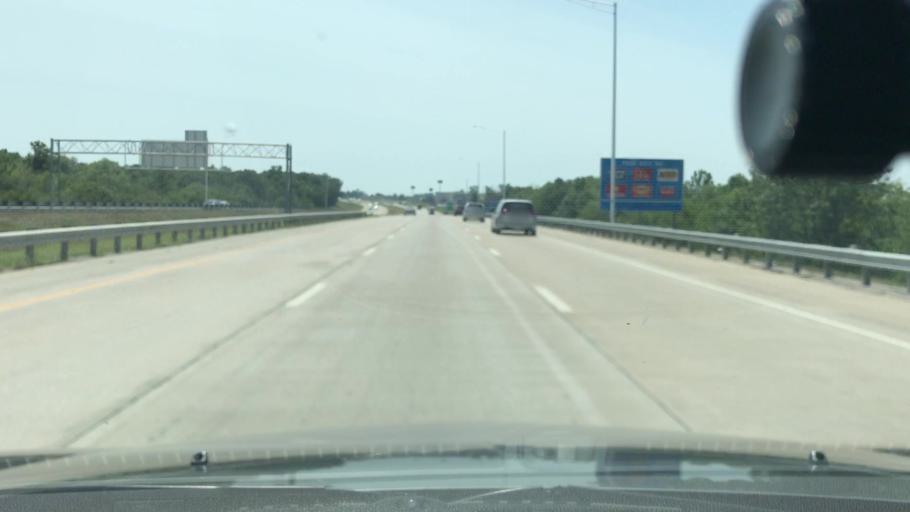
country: US
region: Illinois
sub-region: Jefferson County
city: Mount Vernon
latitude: 38.3274
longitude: -88.9561
